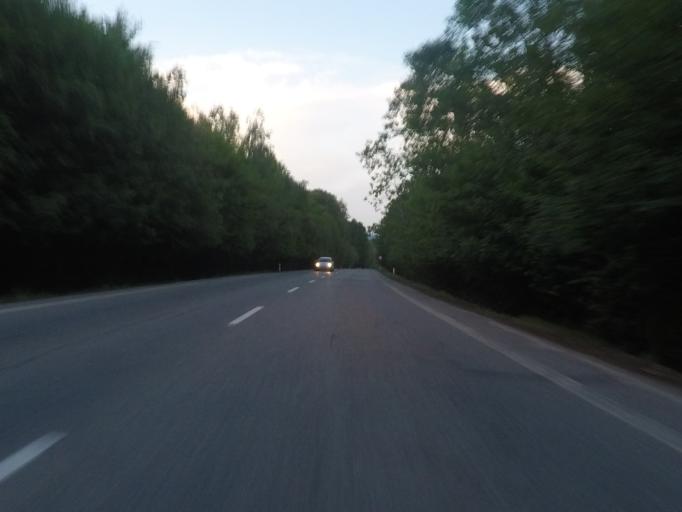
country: SK
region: Banskobystricky
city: Tisovec
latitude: 48.5245
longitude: 19.9463
